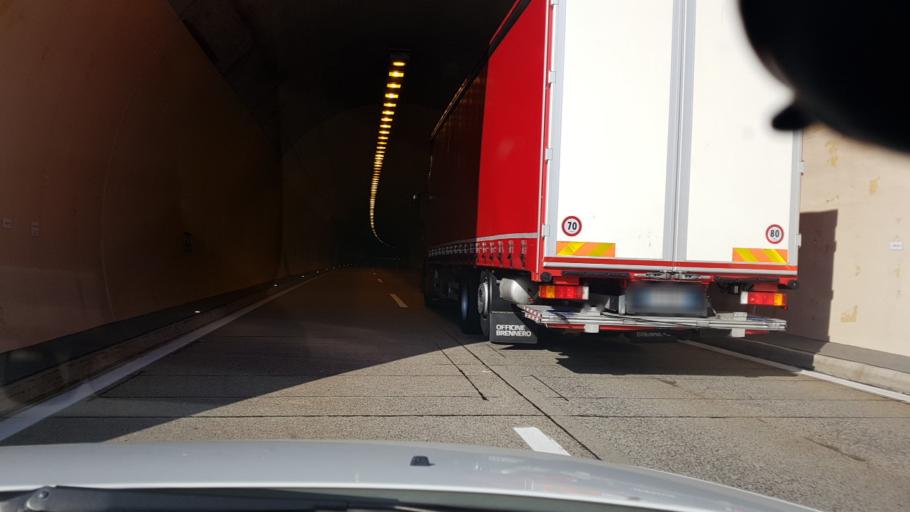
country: AT
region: Carinthia
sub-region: Politischer Bezirk Villach Land
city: Fresach
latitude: 46.6617
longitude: 13.7244
